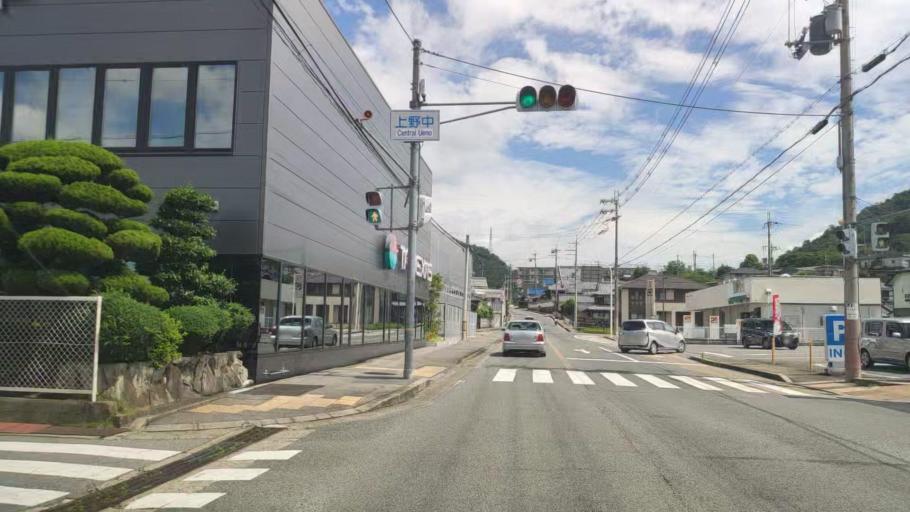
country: JP
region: Hyogo
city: Nishiwaki
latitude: 34.9874
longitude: 134.9786
